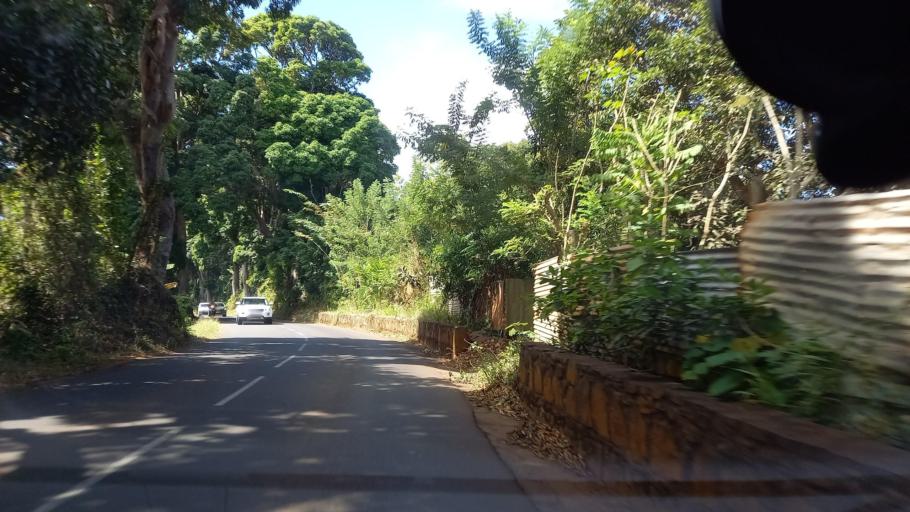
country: YT
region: Mamoudzou
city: Mamoudzou
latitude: -12.7928
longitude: 45.1851
